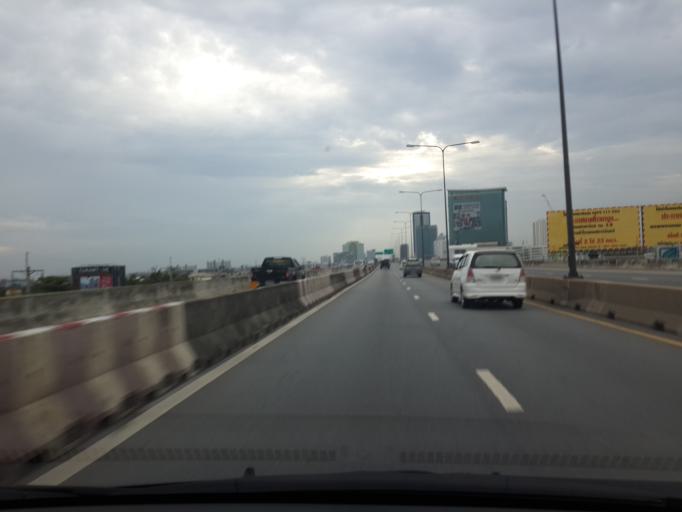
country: TH
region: Bangkok
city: Bang Na
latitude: 13.6649
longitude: 100.6486
